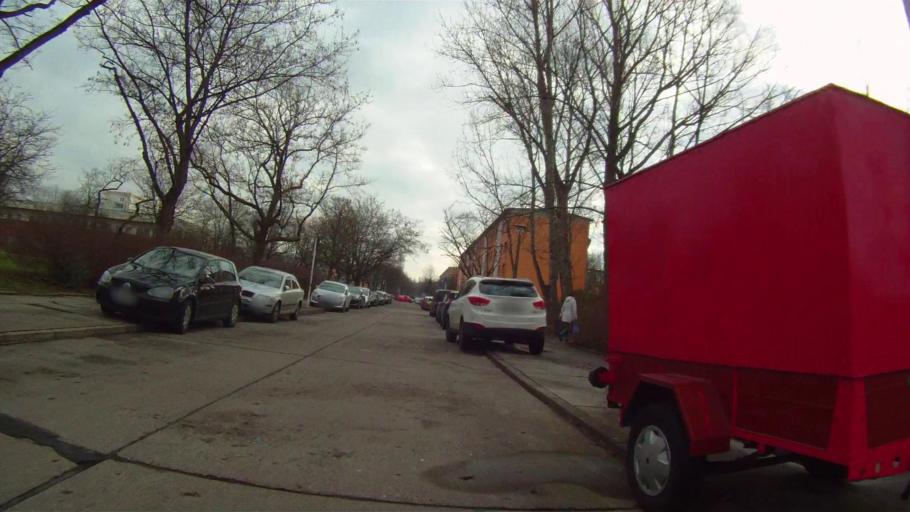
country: DE
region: Berlin
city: Friedrichsfelde
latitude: 52.4991
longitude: 13.5055
